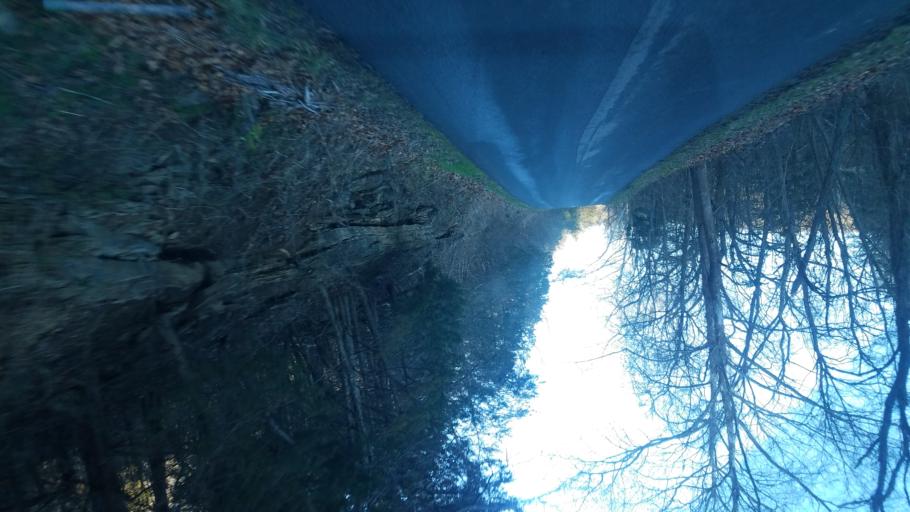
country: US
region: Virginia
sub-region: Pulaski County
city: Pulaski
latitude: 37.1846
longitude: -80.8366
